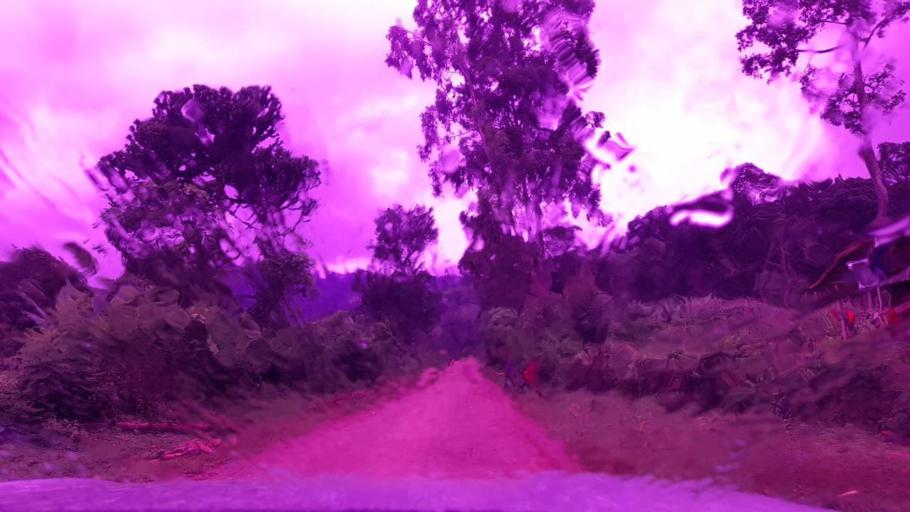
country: ET
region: Southern Nations, Nationalities, and People's Region
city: Bonga
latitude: 7.5605
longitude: 35.8403
